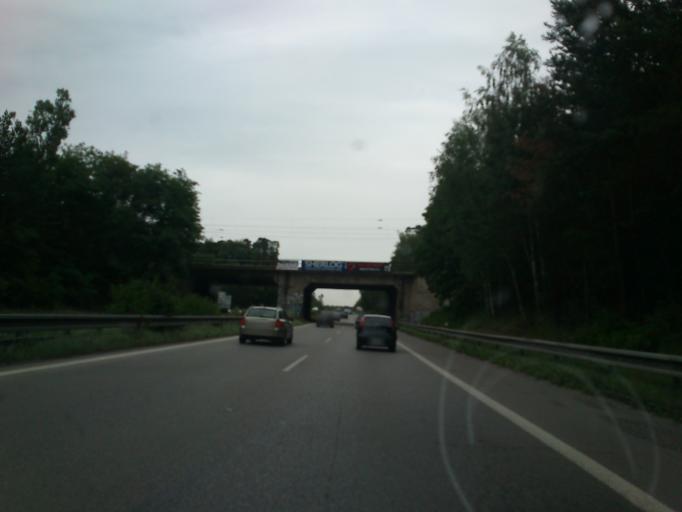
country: CZ
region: Central Bohemia
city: Brandys nad Labem-Stara Boleslav
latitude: 50.2067
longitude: 14.6958
